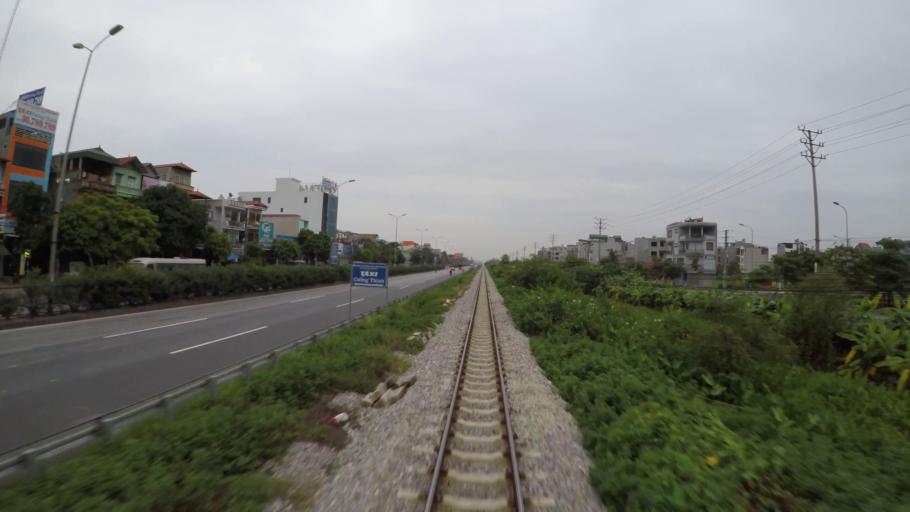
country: VN
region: Hung Yen
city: Nhu Quynh
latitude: 20.9830
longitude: 105.9797
